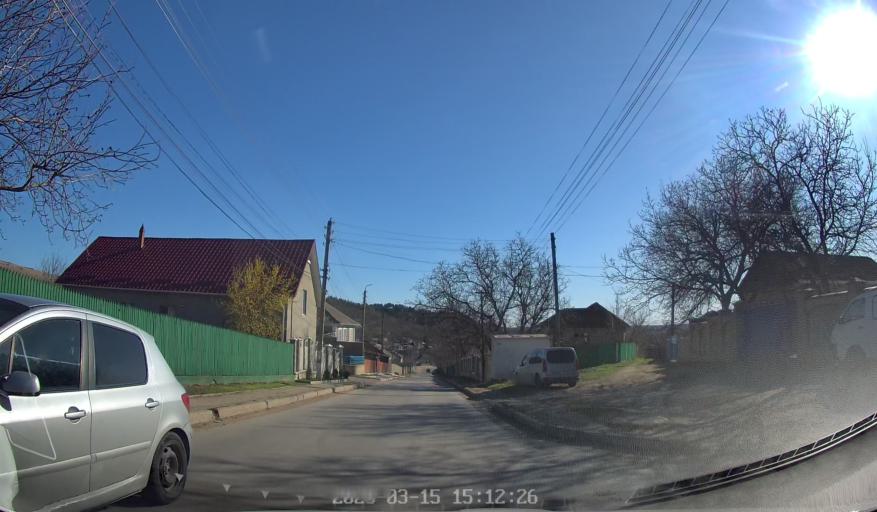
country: MD
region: Orhei
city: Orhei
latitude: 47.2553
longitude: 28.7738
